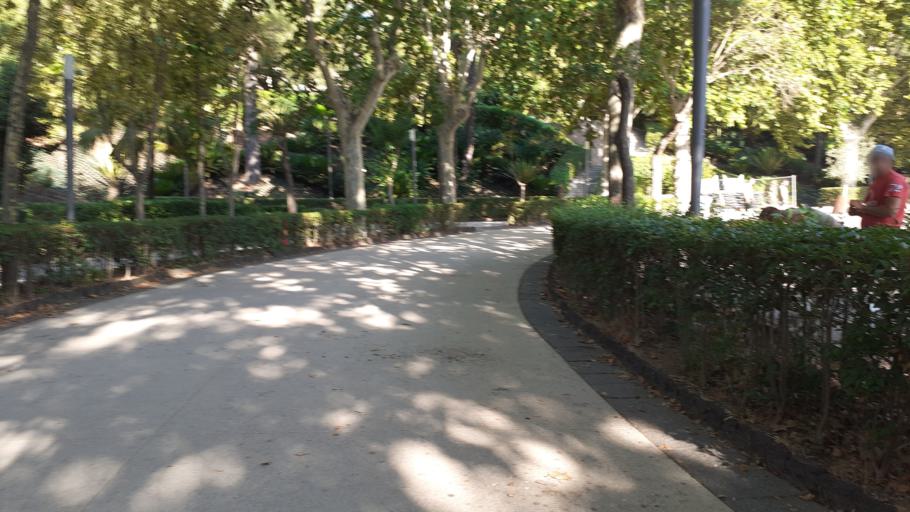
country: IT
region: Sicily
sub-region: Catania
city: Catania
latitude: 37.5109
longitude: 15.0832
